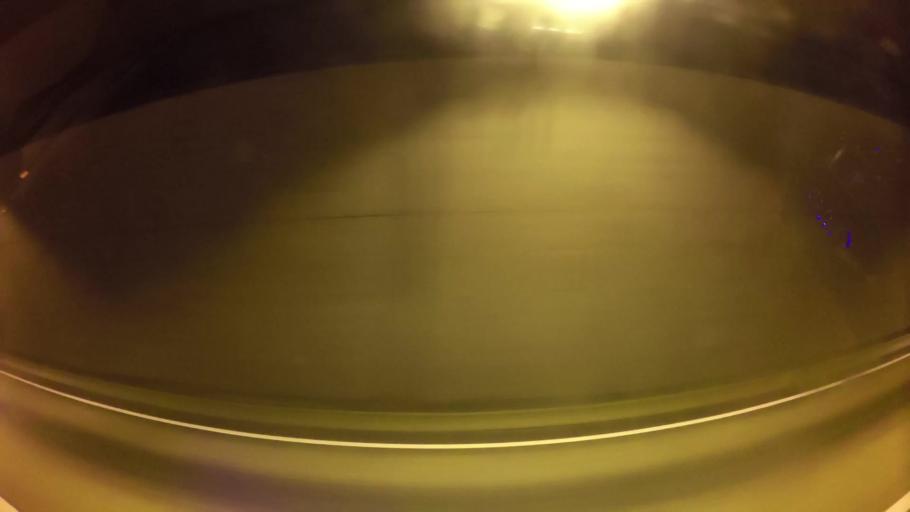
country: CL
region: Valparaiso
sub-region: Provincia de Valparaiso
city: Valparaiso
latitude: -33.0317
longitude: -71.6328
